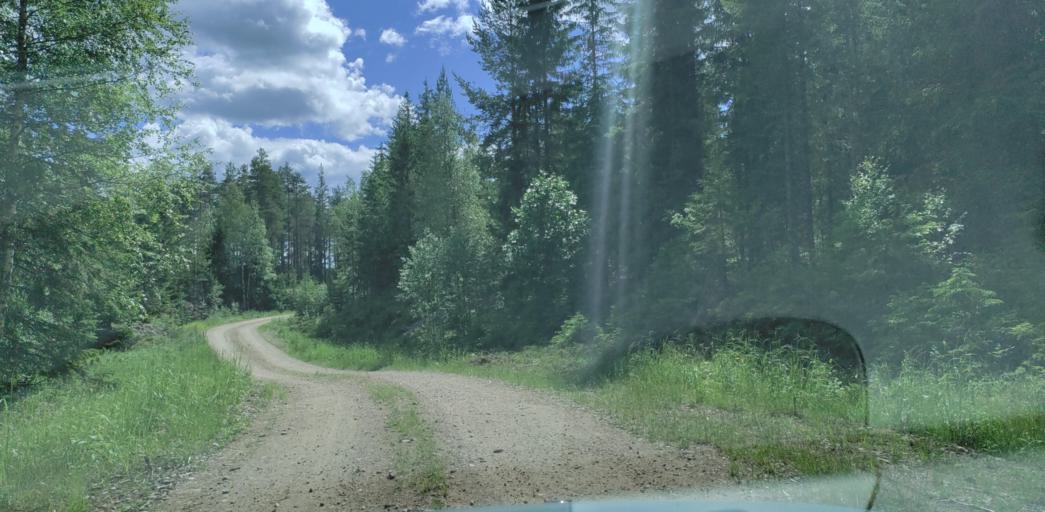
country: SE
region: Vaermland
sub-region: Hagfors Kommun
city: Ekshaerad
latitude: 60.1127
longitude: 13.3248
